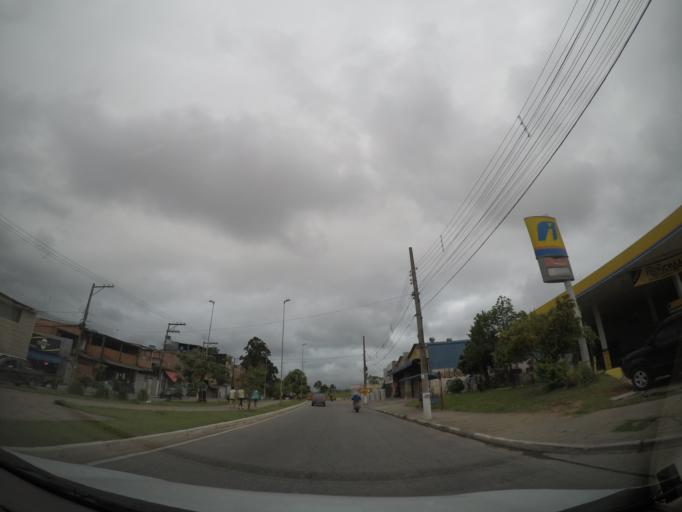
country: BR
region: Sao Paulo
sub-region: Guarulhos
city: Guarulhos
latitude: -23.4072
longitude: -46.4491
